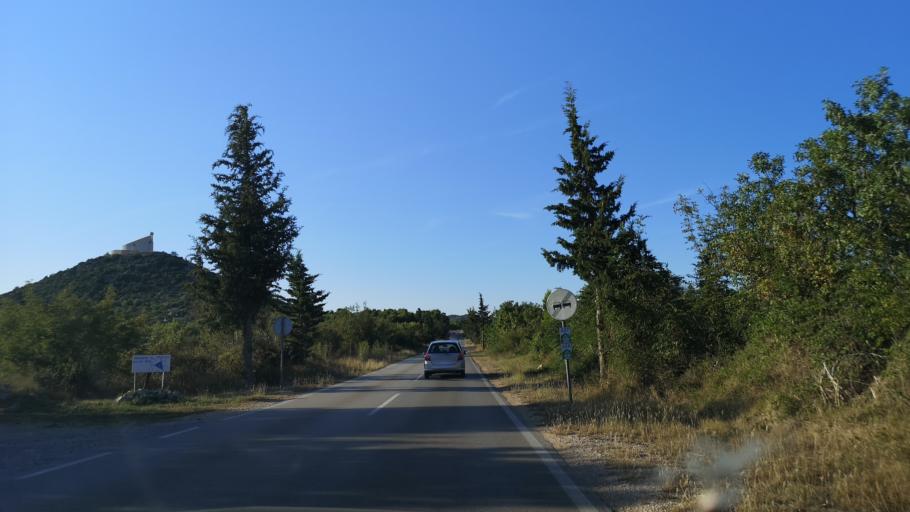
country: HR
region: Sibensko-Kniniska
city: Vodice
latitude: 43.7809
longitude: 15.7733
